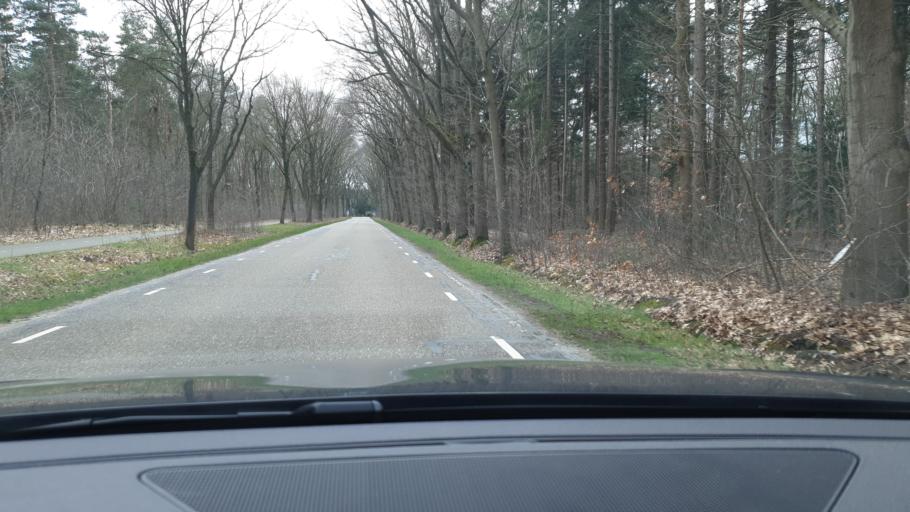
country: NL
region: North Brabant
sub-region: Gemeente Oirschot
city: Oostelbeers
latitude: 51.4248
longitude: 5.2995
